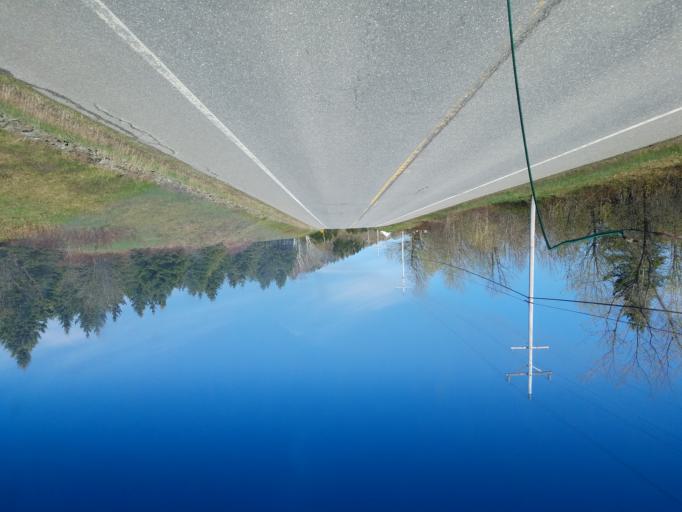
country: US
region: Maine
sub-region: Aroostook County
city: Presque Isle
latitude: 46.6666
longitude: -68.2189
